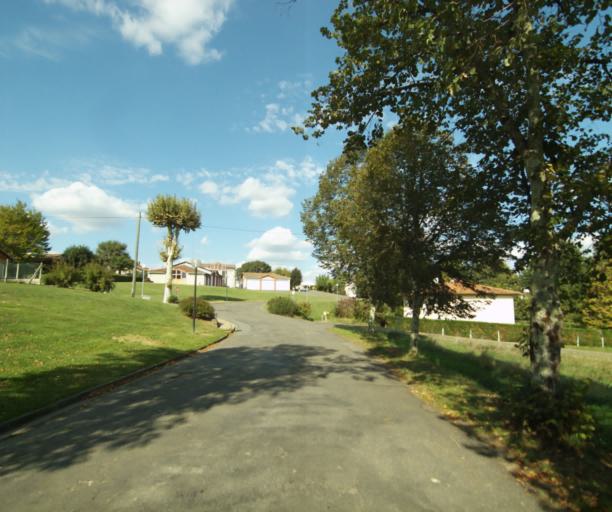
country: FR
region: Midi-Pyrenees
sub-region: Departement du Gers
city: Cazaubon
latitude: 43.9329
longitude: -0.0655
